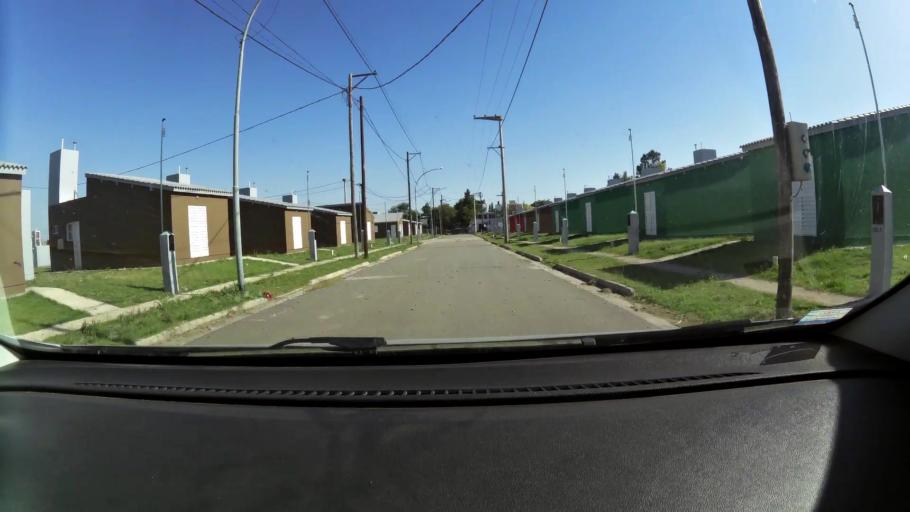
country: AR
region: Cordoba
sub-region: Departamento de Capital
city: Cordoba
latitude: -31.3563
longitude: -64.1940
